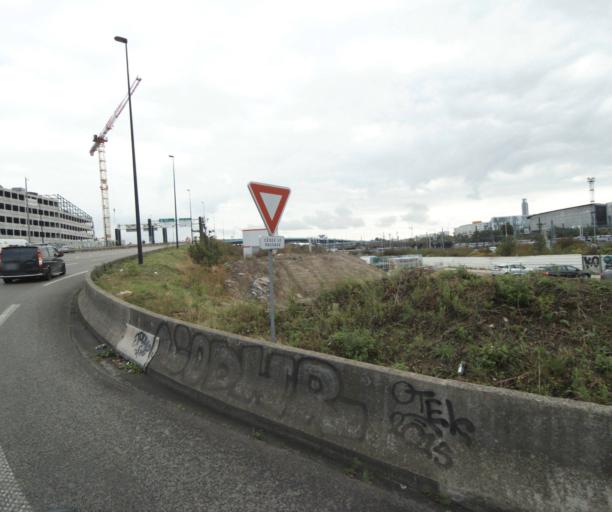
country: FR
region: Nord-Pas-de-Calais
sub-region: Departement du Nord
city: La Madeleine
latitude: 50.6355
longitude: 3.0801
